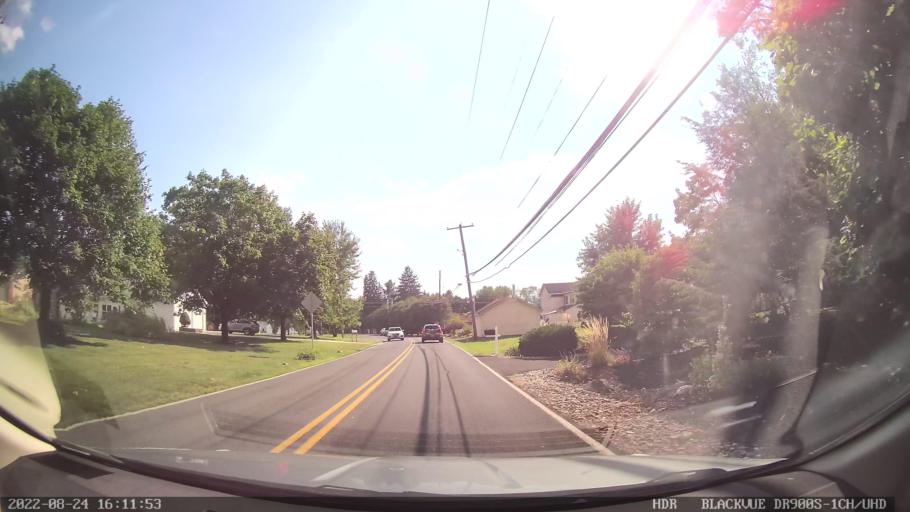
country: US
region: Pennsylvania
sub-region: Lehigh County
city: Wescosville
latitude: 40.5576
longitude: -75.5364
